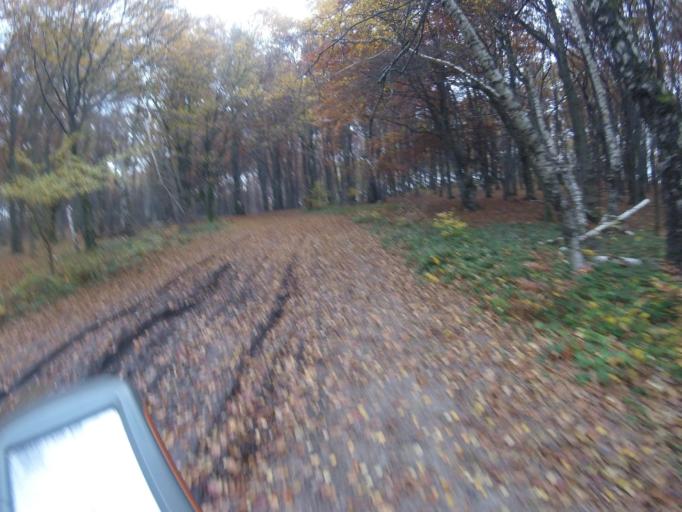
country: HU
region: Borsod-Abauj-Zemplen
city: Gonc
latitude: 48.4388
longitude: 21.3195
